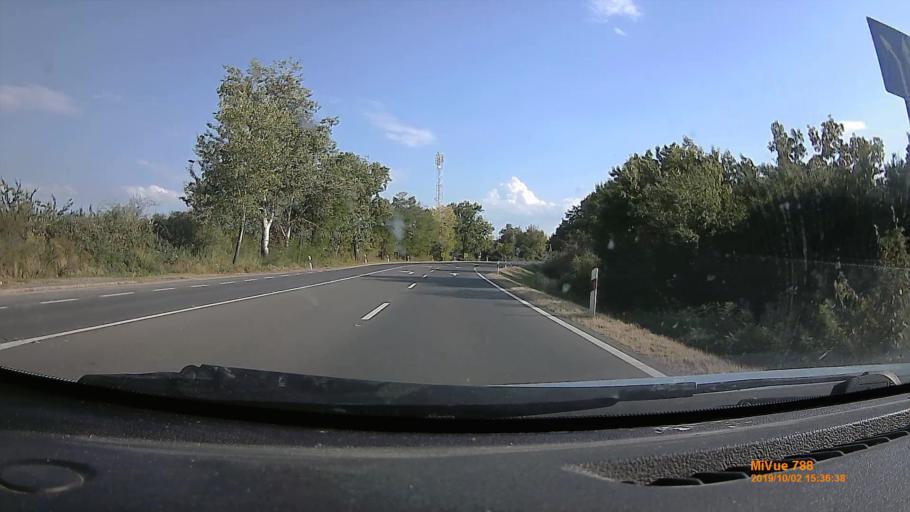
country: HU
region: Heves
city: Egerszalok
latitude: 47.8460
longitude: 20.3722
